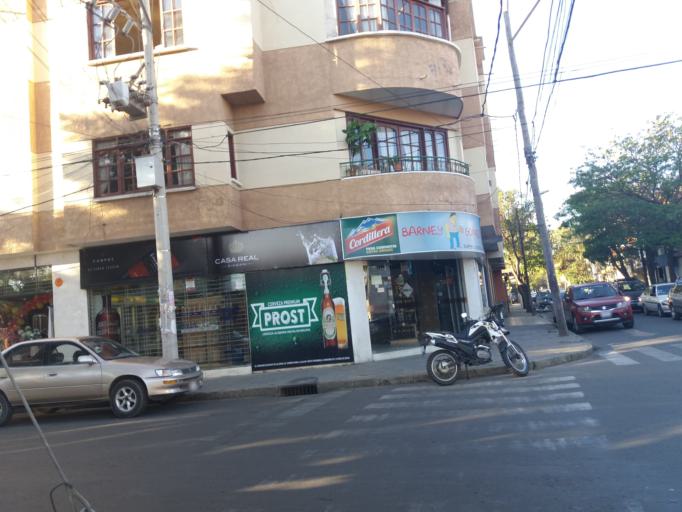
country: BO
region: Tarija
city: Tarija
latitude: -21.5366
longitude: -64.7273
